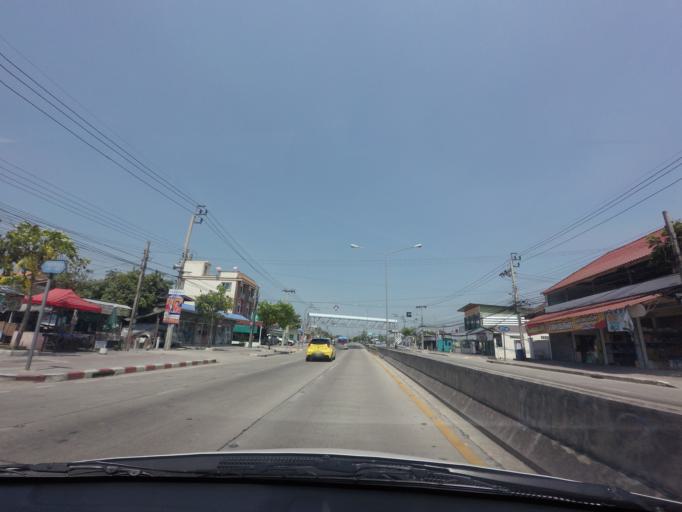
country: TH
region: Bangkok
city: Khlong Sam Wa
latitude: 13.8325
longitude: 100.7732
